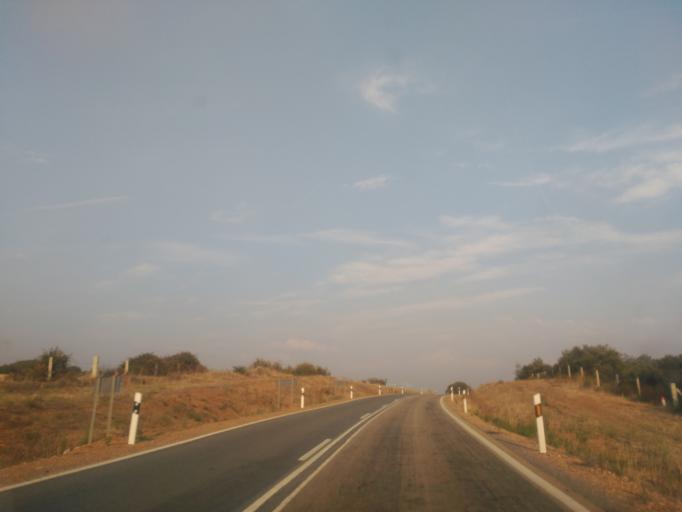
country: ES
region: Castille and Leon
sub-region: Provincia de Zamora
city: Perilla de Castro
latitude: 41.7470
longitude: -5.8434
